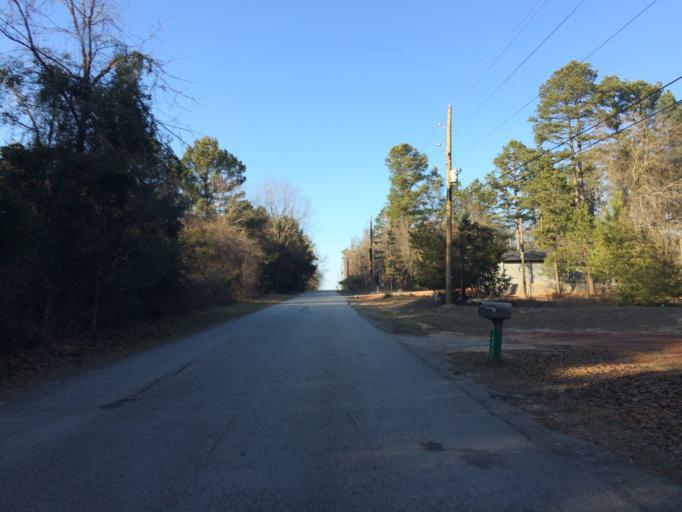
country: US
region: Texas
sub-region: Wood County
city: Hawkins
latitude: 32.7065
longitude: -95.1806
